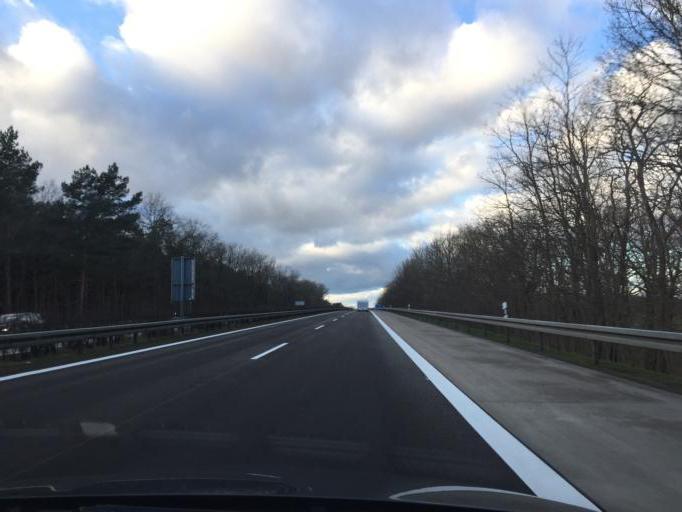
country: DE
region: Brandenburg
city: Lubbenau
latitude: 51.8337
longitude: 13.9745
